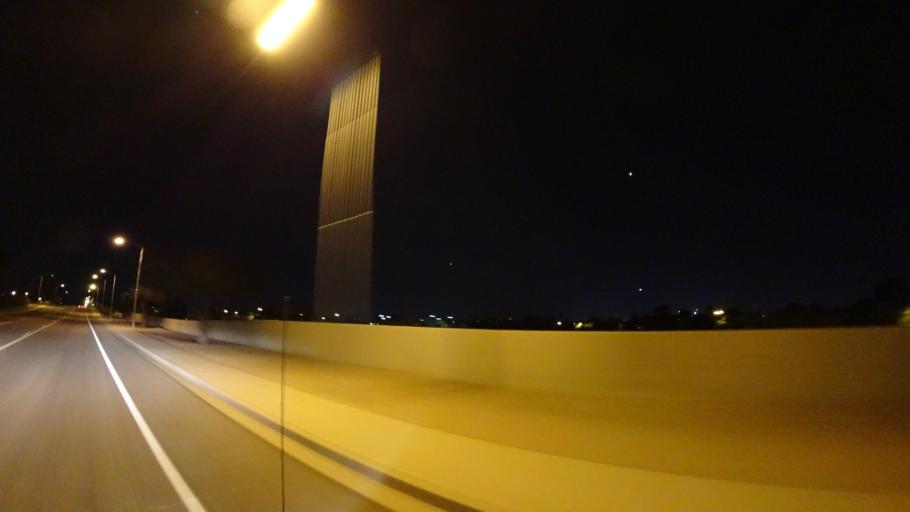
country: US
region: Arizona
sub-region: Maricopa County
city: Mesa
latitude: 33.4473
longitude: -111.8138
